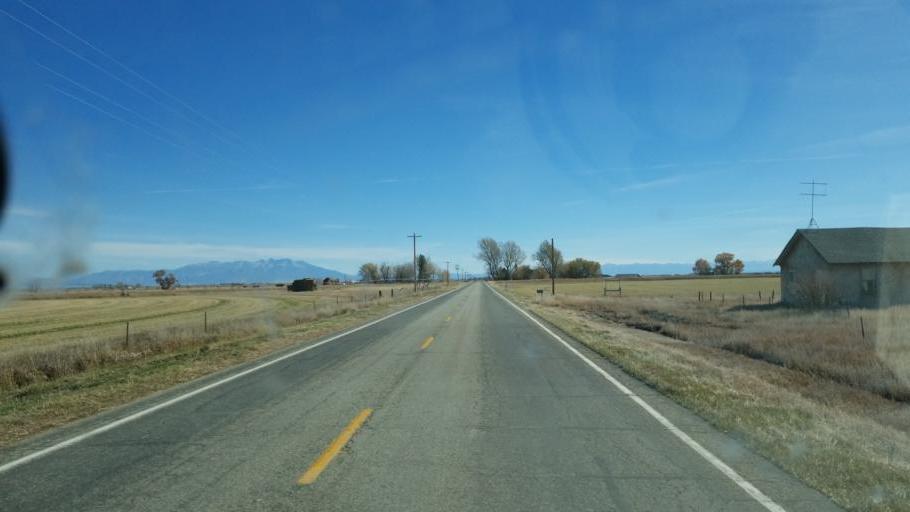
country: US
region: Colorado
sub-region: Rio Grande County
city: Monte Vista
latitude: 37.4300
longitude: -106.1182
